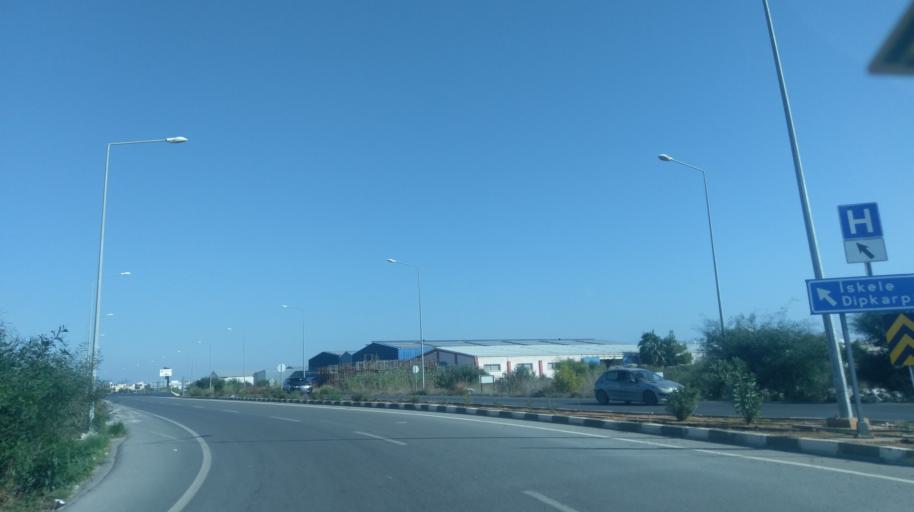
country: CY
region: Ammochostos
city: Famagusta
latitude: 35.1444
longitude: 33.8956
